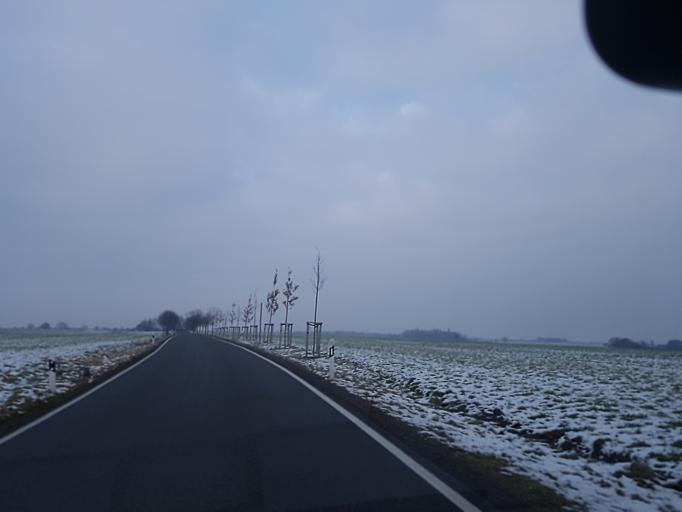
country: DE
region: Saxony
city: Naundorf
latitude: 51.2680
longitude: 13.1045
